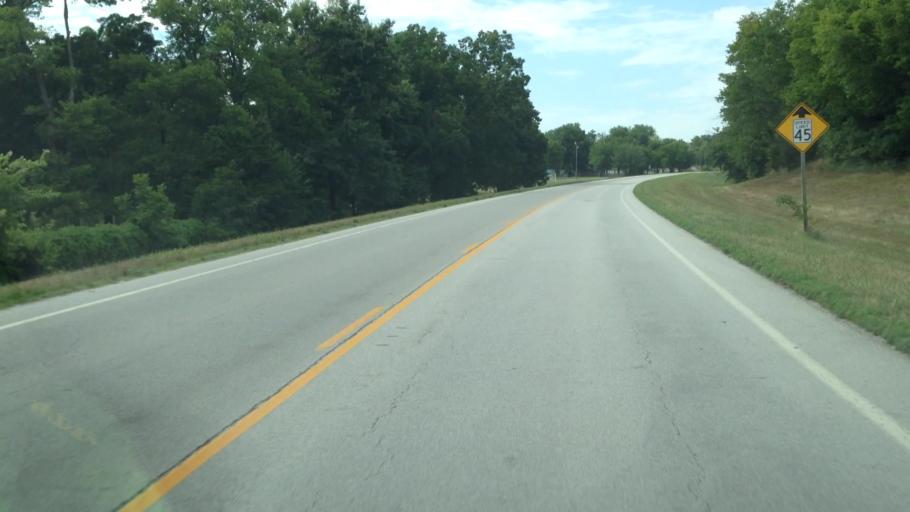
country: US
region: Kansas
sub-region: Labette County
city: Oswego
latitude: 37.1537
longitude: -95.1075
